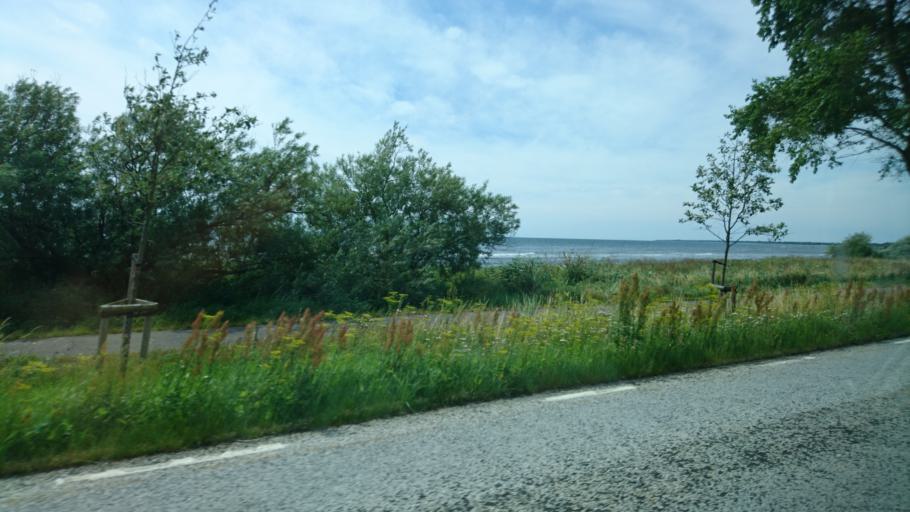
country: SE
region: Skane
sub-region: Skurups Kommun
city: Skivarp
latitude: 55.3878
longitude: 13.5437
